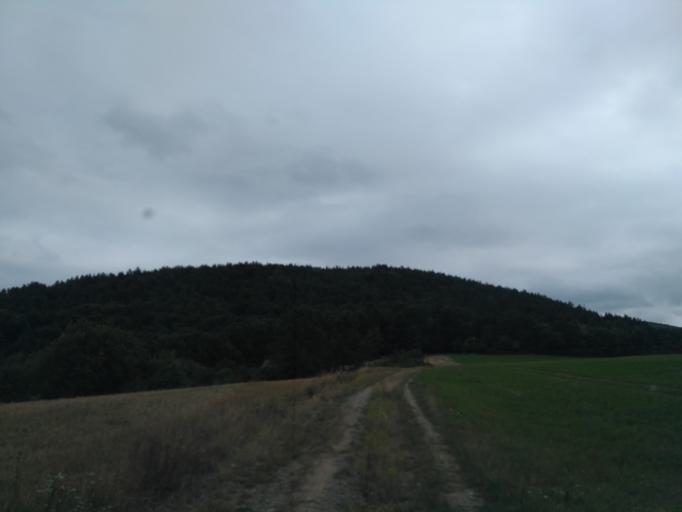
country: SK
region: Presovsky
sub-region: Okres Presov
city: Presov
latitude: 48.9021
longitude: 21.1614
